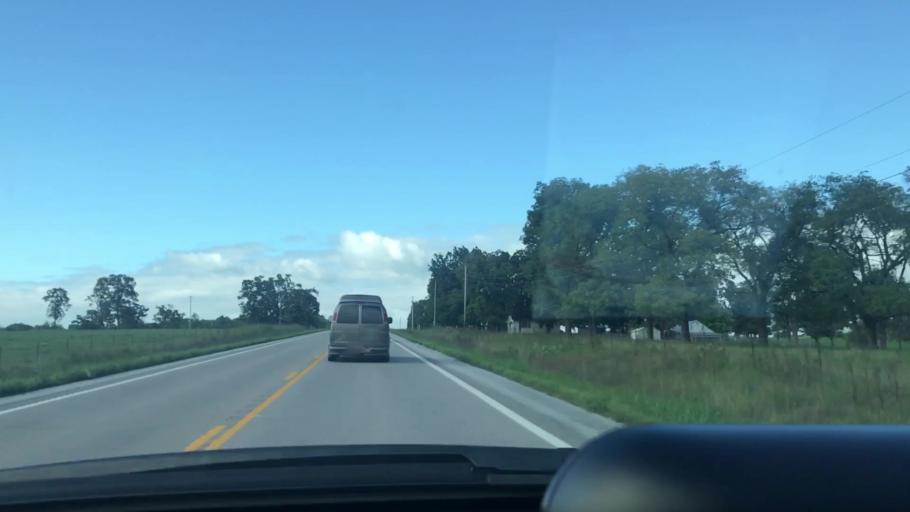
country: US
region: Missouri
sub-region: Hickory County
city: Hermitage
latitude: 37.9718
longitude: -93.2063
